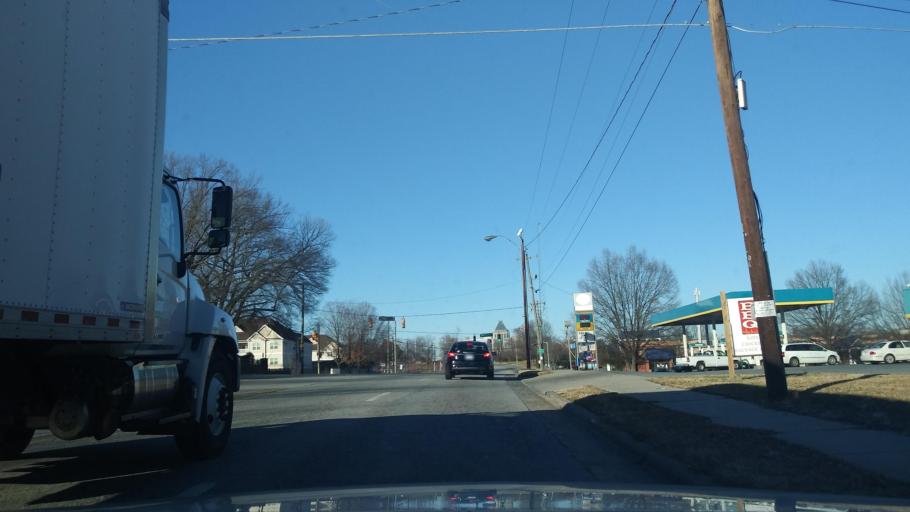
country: US
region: North Carolina
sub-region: Guilford County
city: Greensboro
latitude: 36.0581
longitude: -79.7937
